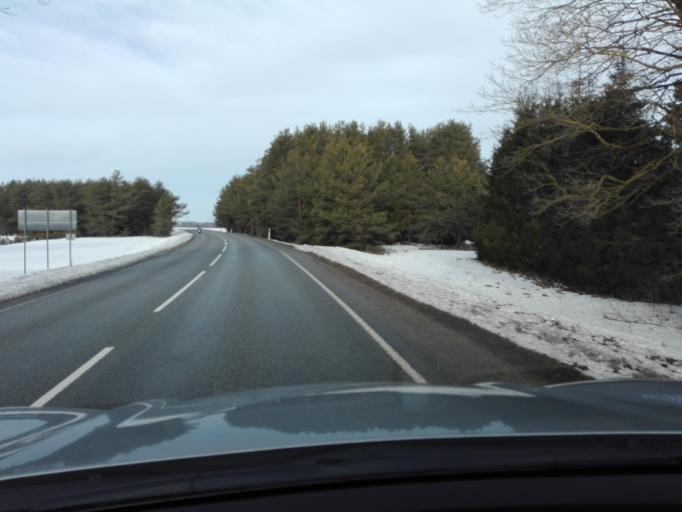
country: EE
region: Raplamaa
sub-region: Kehtna vald
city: Kehtna
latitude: 58.9012
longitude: 24.7873
